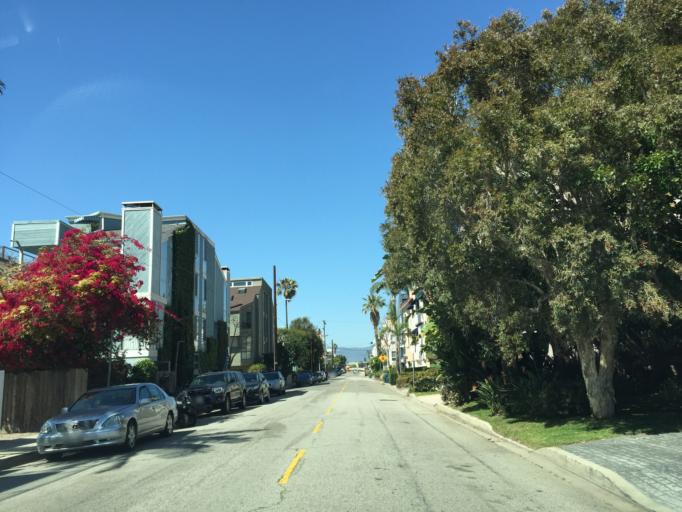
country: US
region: California
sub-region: Los Angeles County
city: Marina del Rey
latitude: 33.9669
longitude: -118.4560
